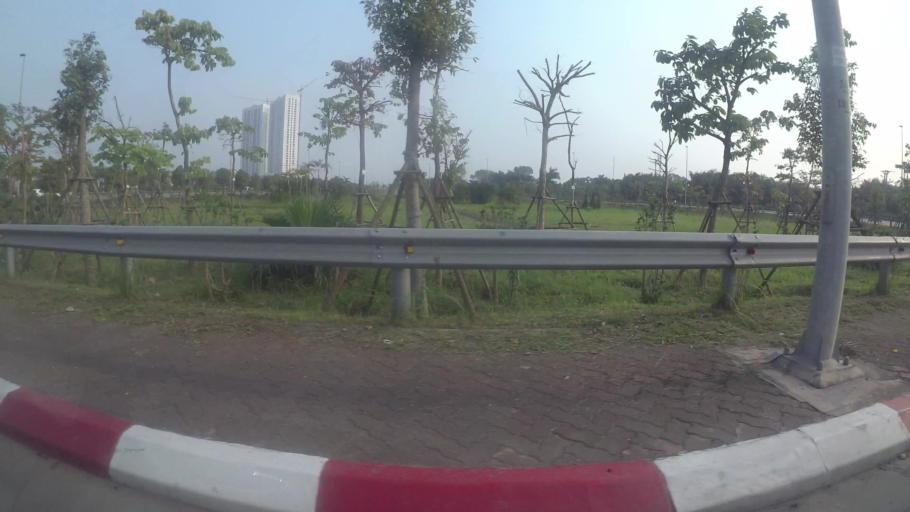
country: VN
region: Ha Noi
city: Dong Anh
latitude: 21.1176
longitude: 105.8266
